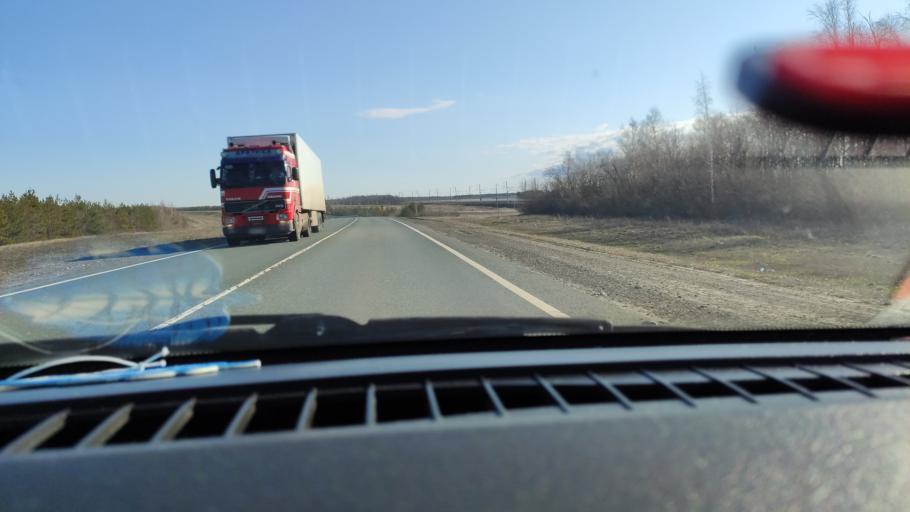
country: RU
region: Samara
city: Syzran'
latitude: 52.8726
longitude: 48.2866
